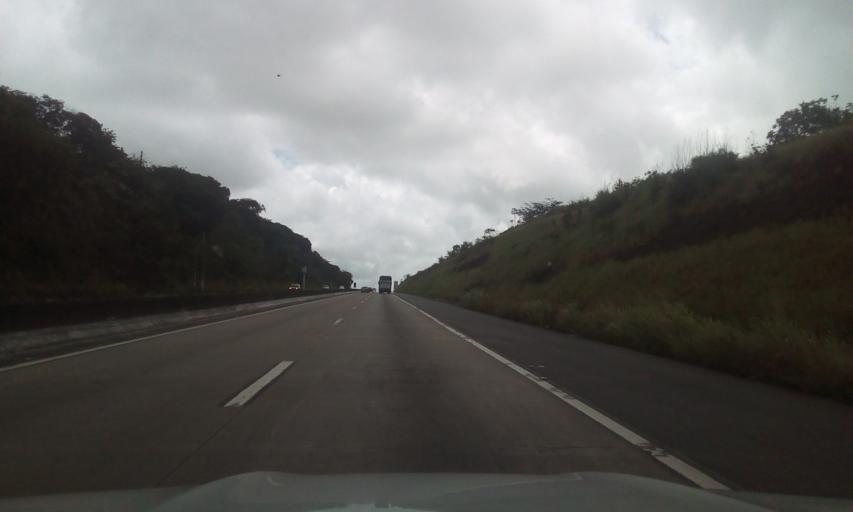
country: BR
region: Pernambuco
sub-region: Itapissuma
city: Itapissuma
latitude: -7.6831
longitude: -34.9243
